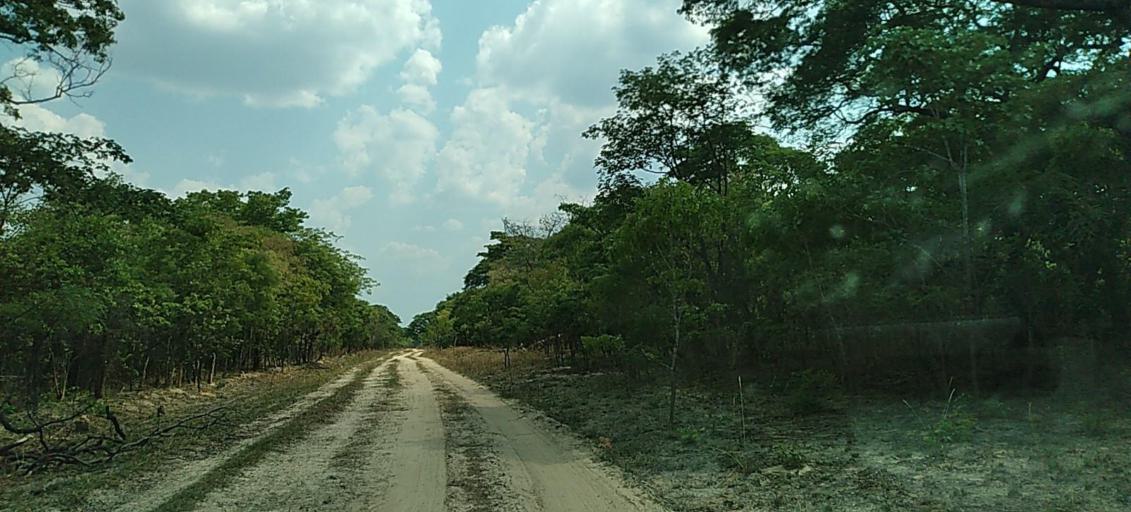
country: ZM
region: Copperbelt
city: Mpongwe
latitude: -13.8439
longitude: 27.9344
